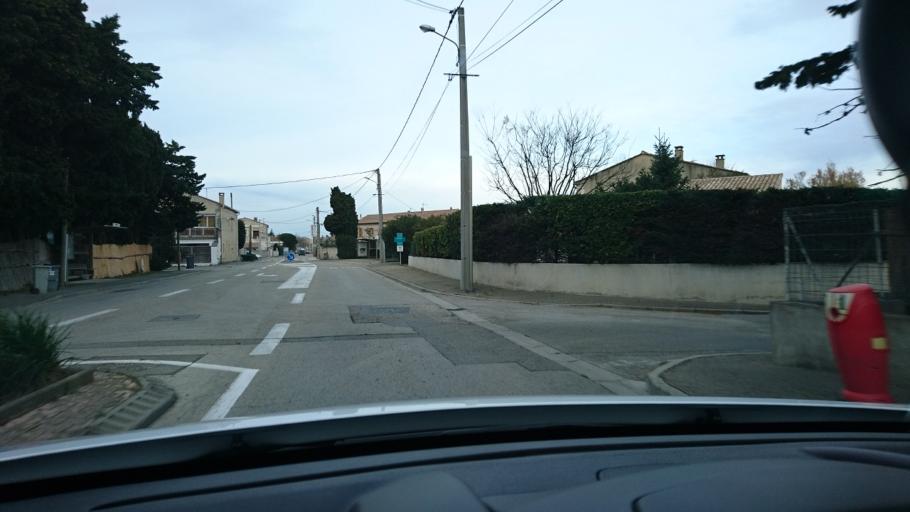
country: FR
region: Provence-Alpes-Cote d'Azur
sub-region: Departement des Bouches-du-Rhone
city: Rognonas
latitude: 43.8956
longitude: 4.8076
